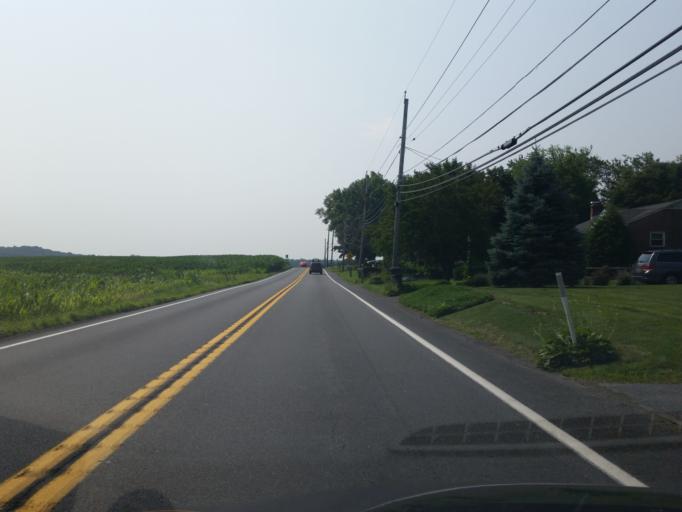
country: US
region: Pennsylvania
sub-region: Dauphin County
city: Palmdale
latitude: 40.3314
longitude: -76.6384
